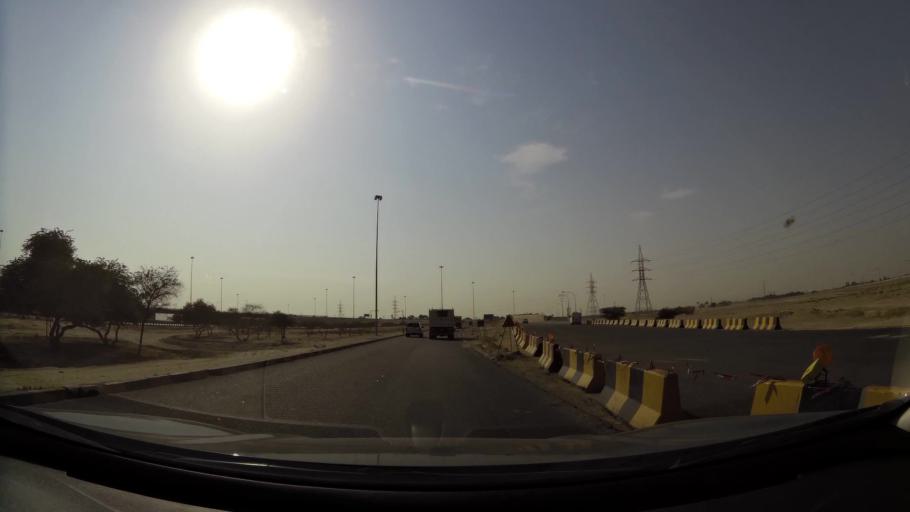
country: KW
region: Al Ahmadi
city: Al Ahmadi
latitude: 28.9610
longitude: 48.1200
